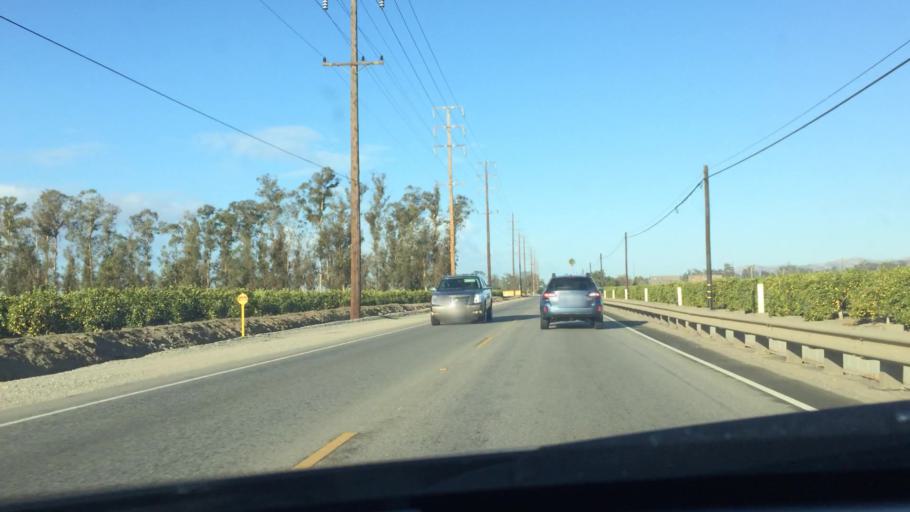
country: US
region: California
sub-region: Ventura County
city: Saticoy
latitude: 34.2637
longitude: -119.0868
